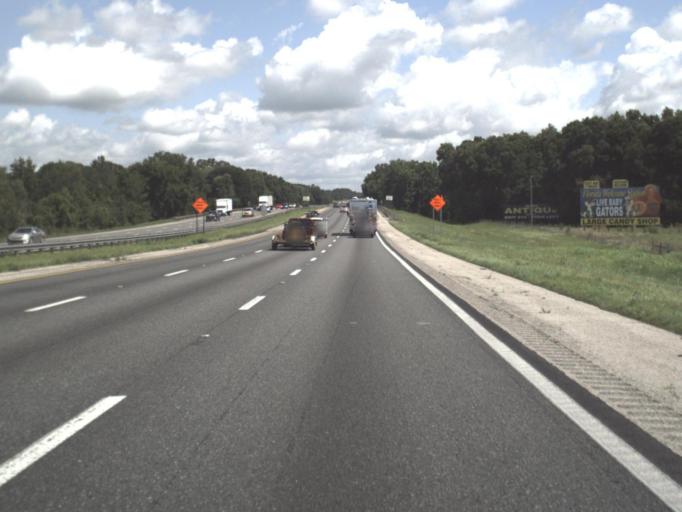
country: US
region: Florida
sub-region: Alachua County
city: Alachua
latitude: 29.7719
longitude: -82.5076
